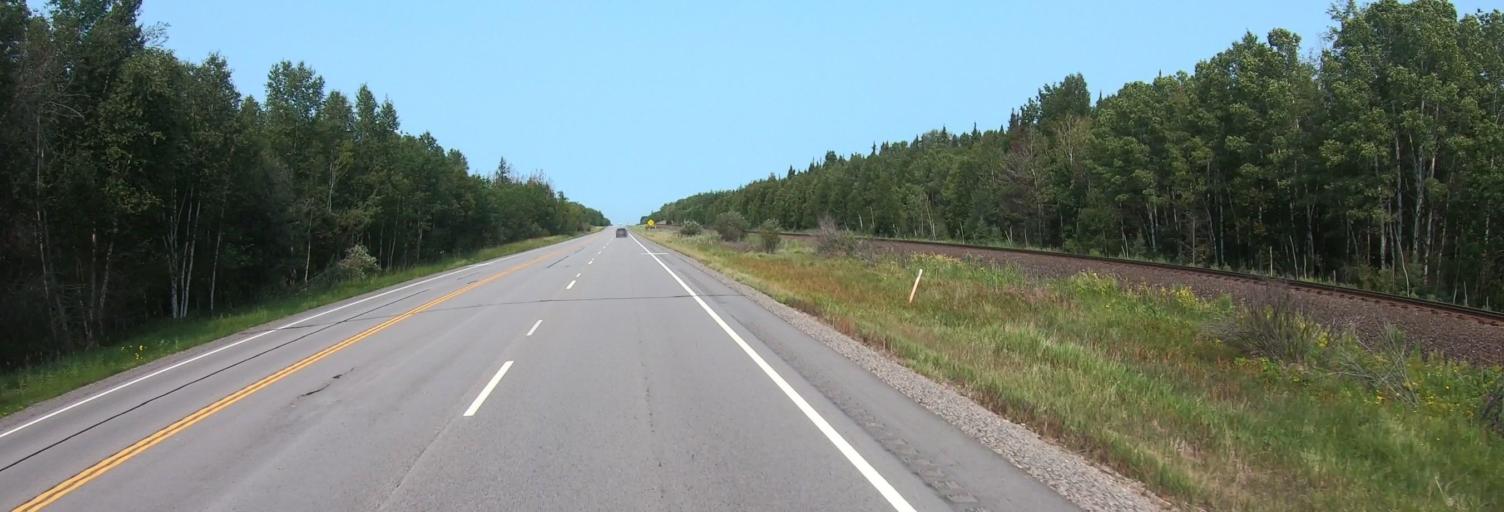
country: CA
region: Ontario
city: Fort Frances
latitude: 48.4574
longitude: -93.2810
